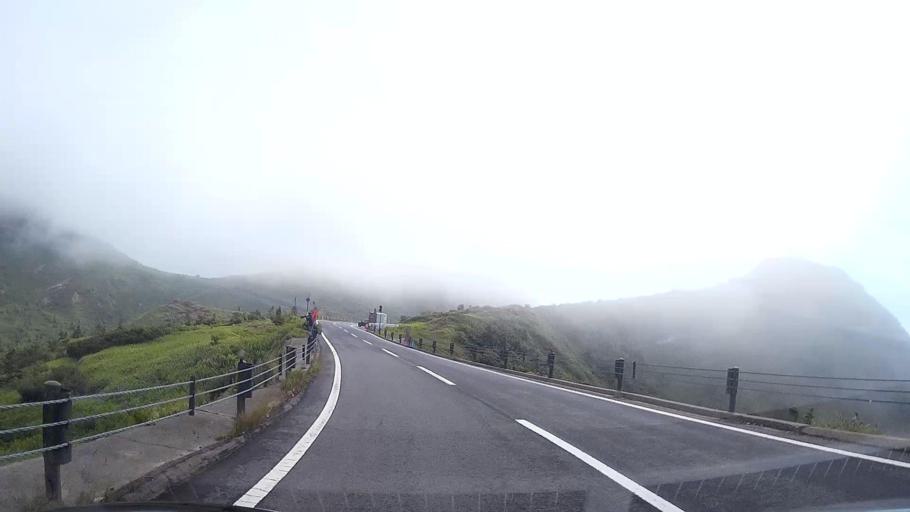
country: JP
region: Nagano
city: Nakano
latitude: 36.6542
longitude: 138.5285
